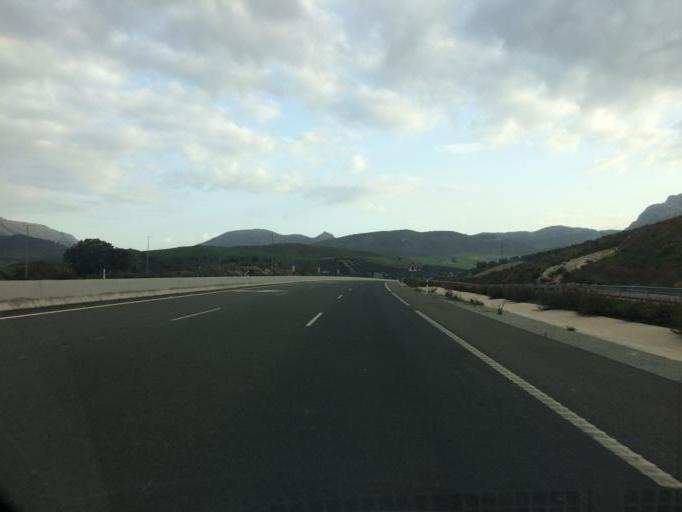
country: ES
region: Andalusia
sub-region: Provincia de Malaga
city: Casabermeja
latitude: 36.9184
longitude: -4.4394
